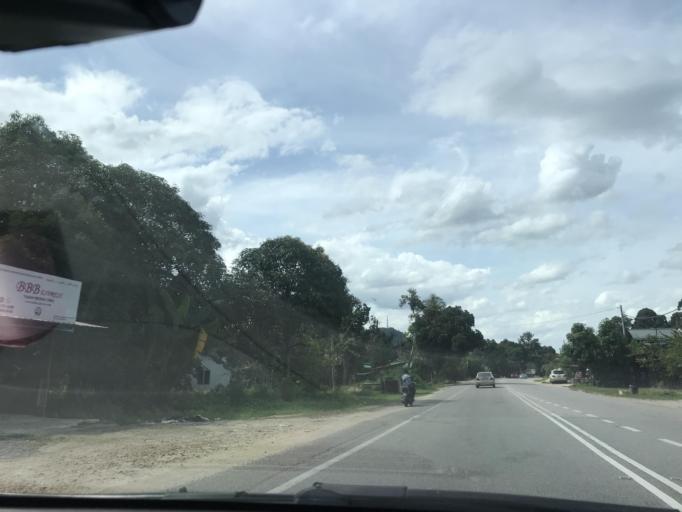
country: MY
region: Kelantan
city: Pulai Chondong
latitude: 5.8696
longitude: 102.1700
